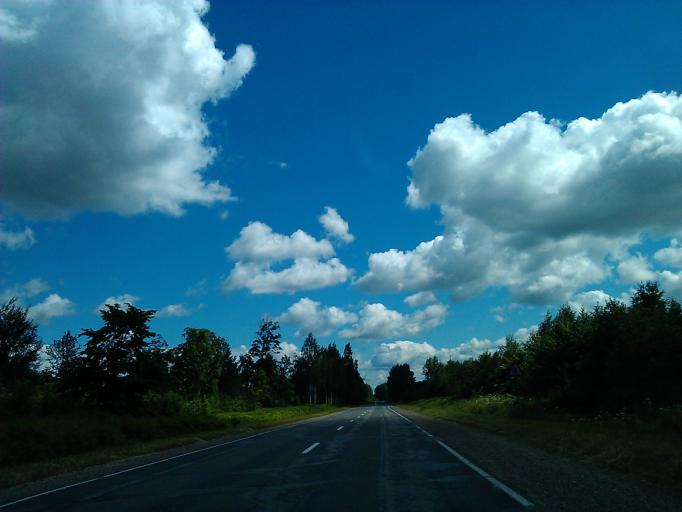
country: LV
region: Varaklani
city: Varaklani
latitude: 56.6092
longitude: 26.7942
